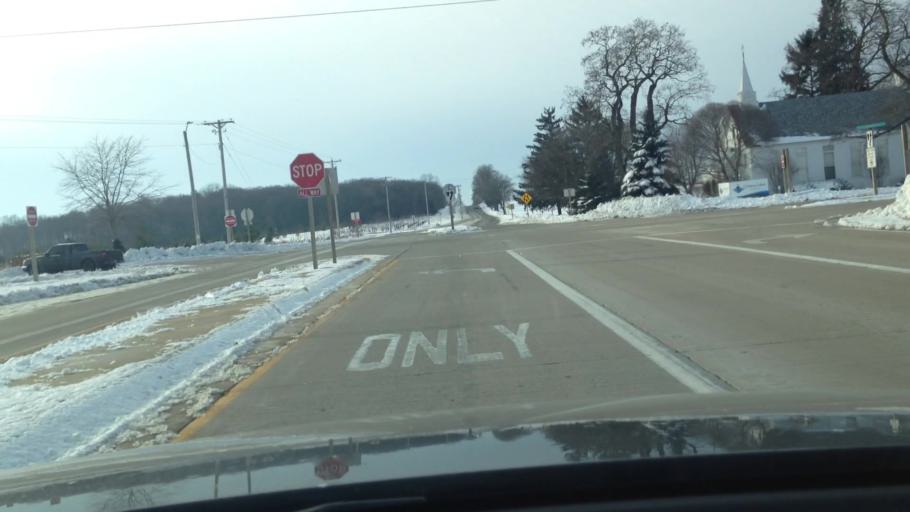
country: US
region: Wisconsin
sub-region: Walworth County
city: Lake Geneva
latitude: 42.5455
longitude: -88.4423
